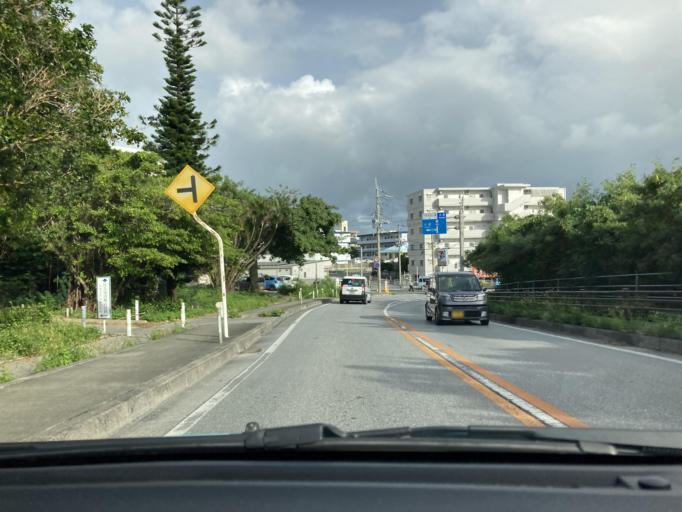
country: JP
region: Okinawa
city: Tomigusuku
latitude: 26.1813
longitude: 127.6628
